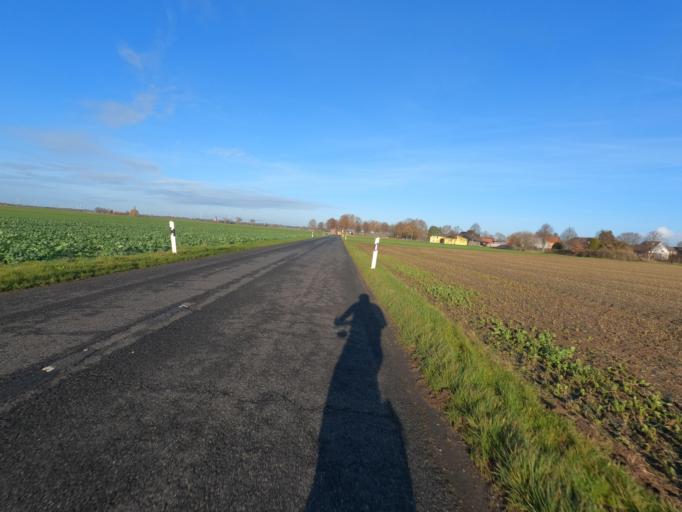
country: DE
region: North Rhine-Westphalia
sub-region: Regierungsbezirk Koln
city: Titz
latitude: 50.9748
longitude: 6.4080
